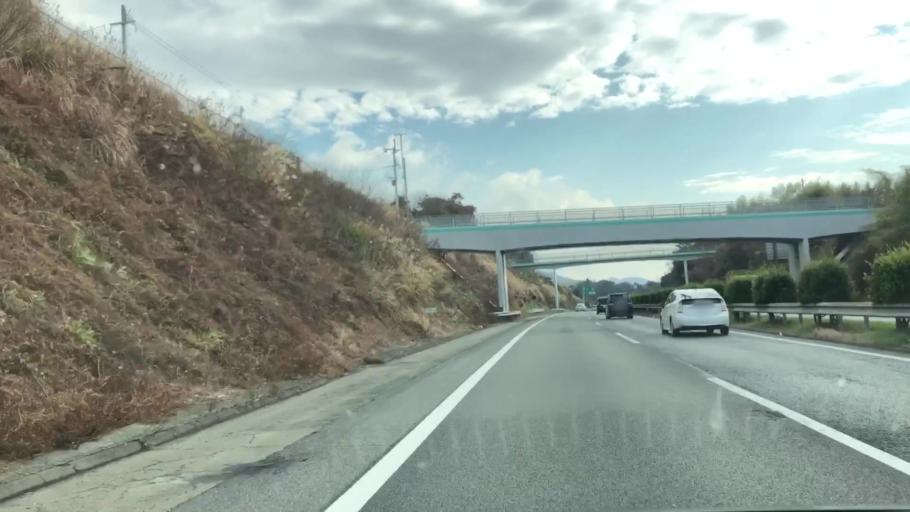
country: JP
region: Fukuoka
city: Setakamachi-takayanagi
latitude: 33.1386
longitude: 130.5141
